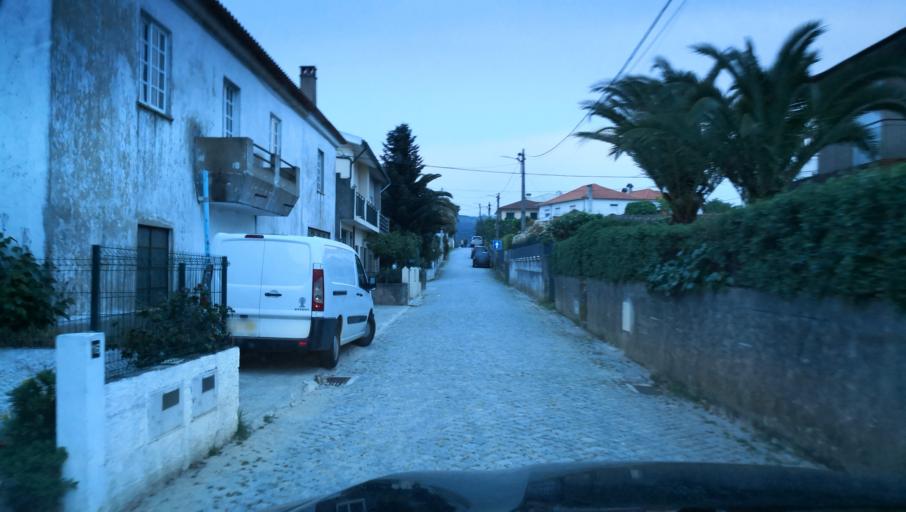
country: PT
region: Vila Real
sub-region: Vila Real
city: Vila Real
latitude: 41.2972
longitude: -7.7234
